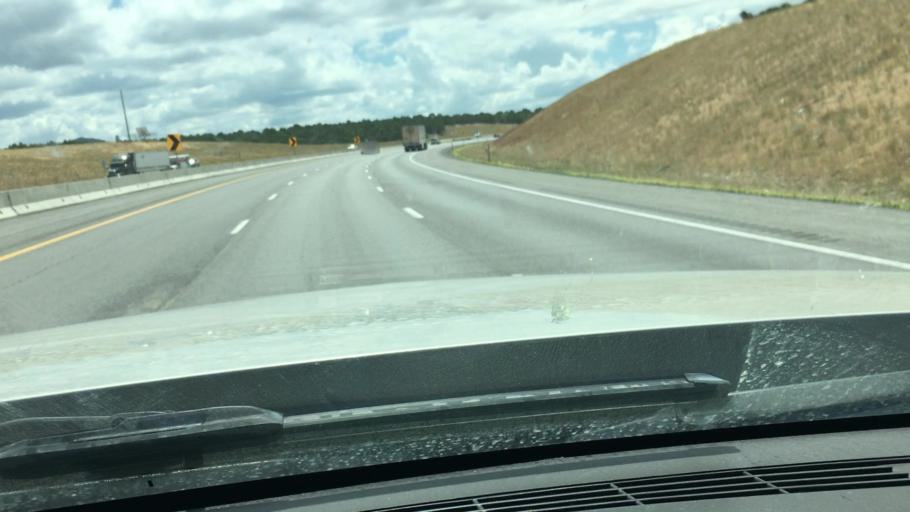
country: US
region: Utah
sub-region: Beaver County
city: Beaver
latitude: 38.4765
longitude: -112.6136
